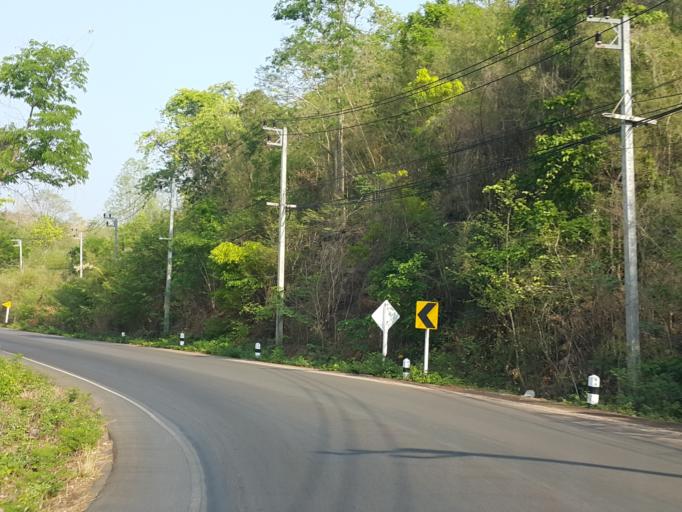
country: TH
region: Kanchanaburi
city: Sai Yok
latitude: 14.1194
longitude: 99.1468
